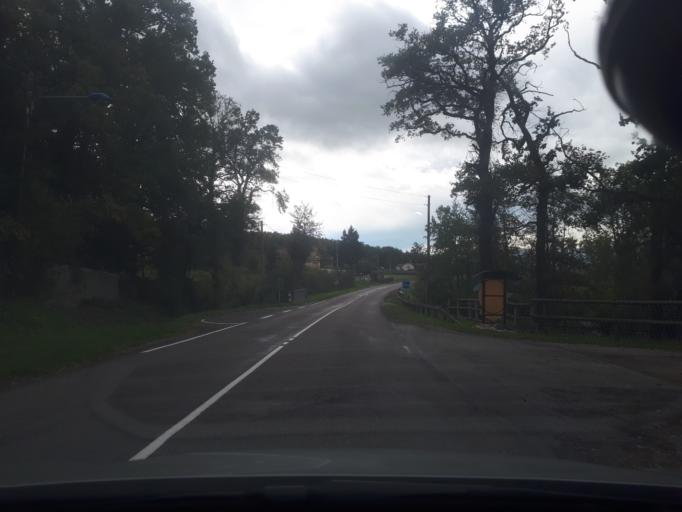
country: FR
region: Rhone-Alpes
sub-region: Departement de la Loire
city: Bellegarde-en-Forez
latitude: 45.6897
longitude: 4.3027
